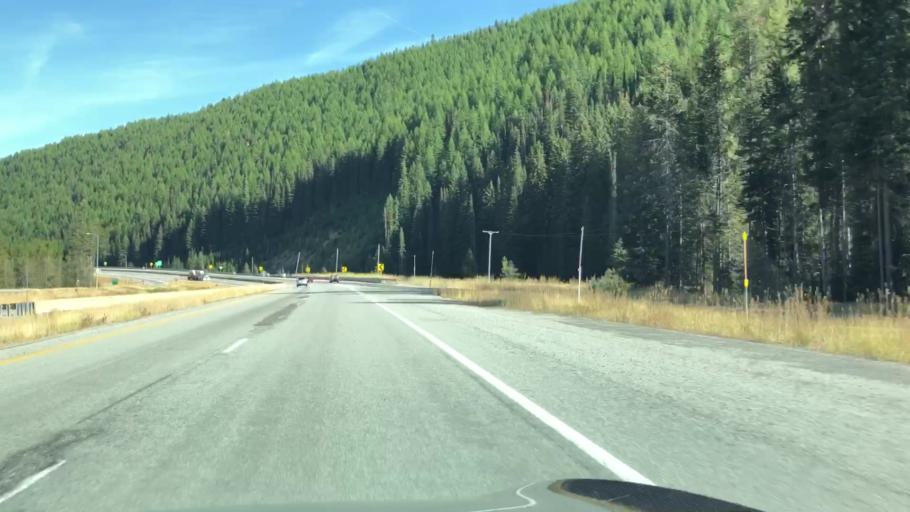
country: US
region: Idaho
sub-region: Shoshone County
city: Wallace
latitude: 47.4191
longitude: -115.6258
